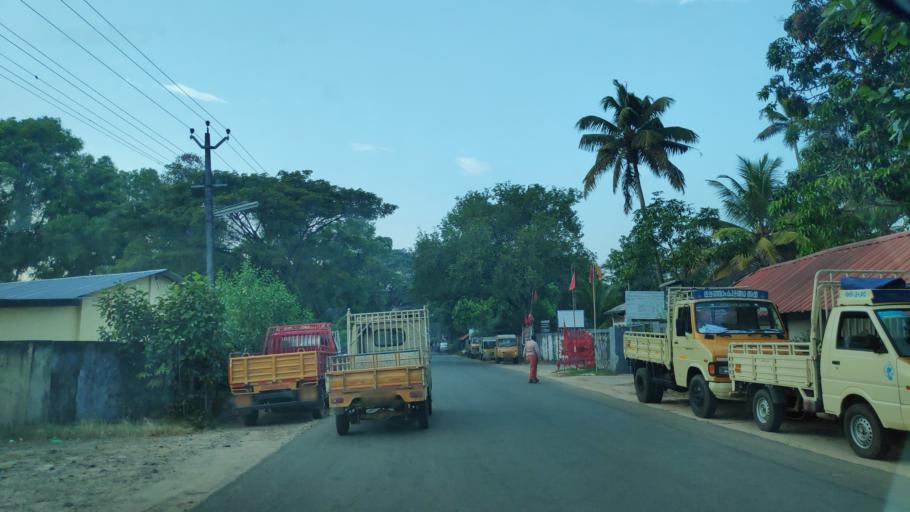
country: IN
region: Kerala
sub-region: Alappuzha
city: Shertallai
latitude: 9.6401
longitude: 76.3713
